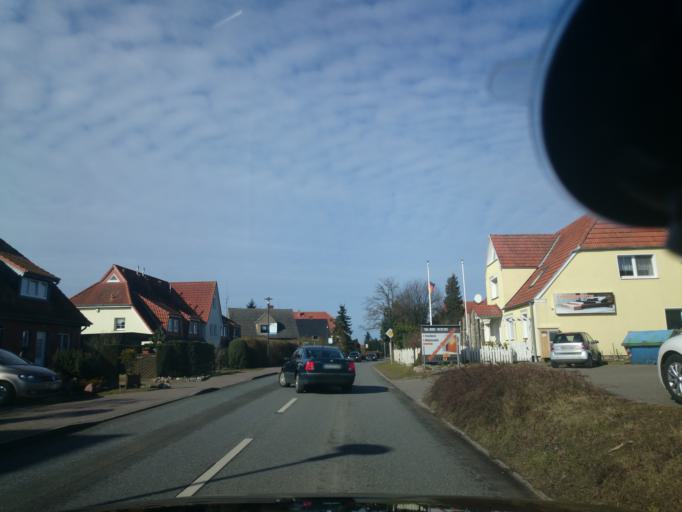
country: DE
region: Mecklenburg-Vorpommern
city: Elmenhorst
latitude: 54.1584
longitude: 12.0029
